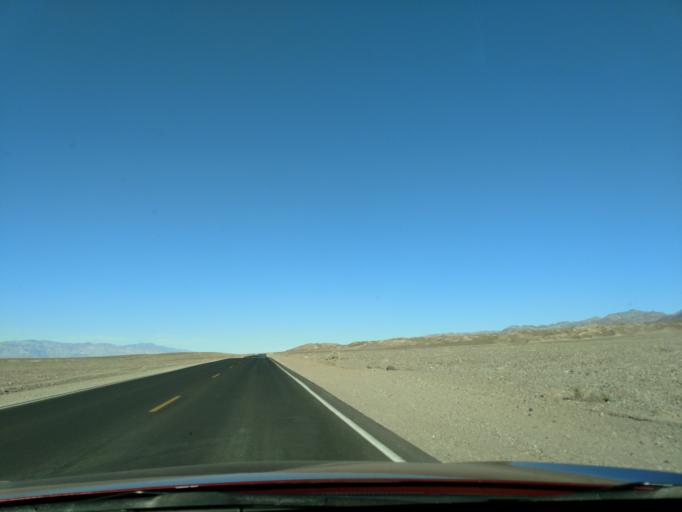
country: US
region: Nevada
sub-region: Nye County
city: Beatty
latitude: 36.6201
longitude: -117.0001
